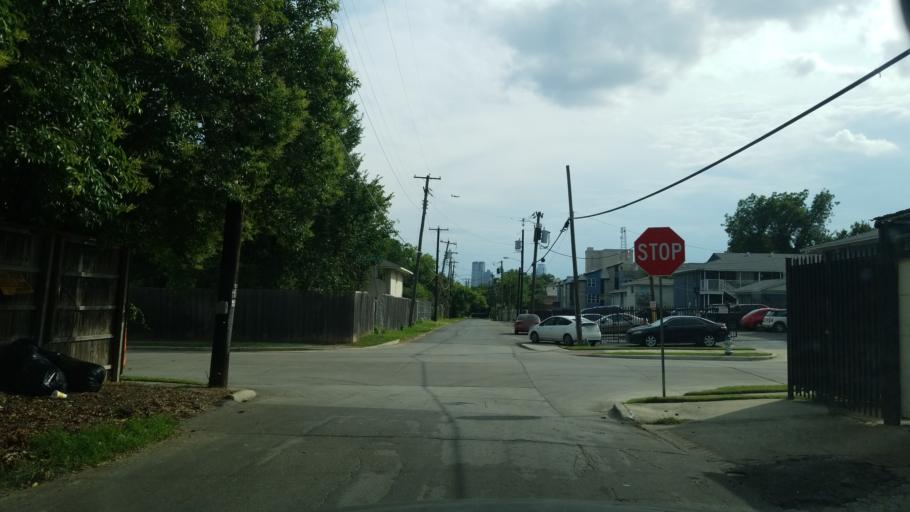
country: US
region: Texas
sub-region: Dallas County
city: Highland Park
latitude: 32.8036
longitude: -96.7697
